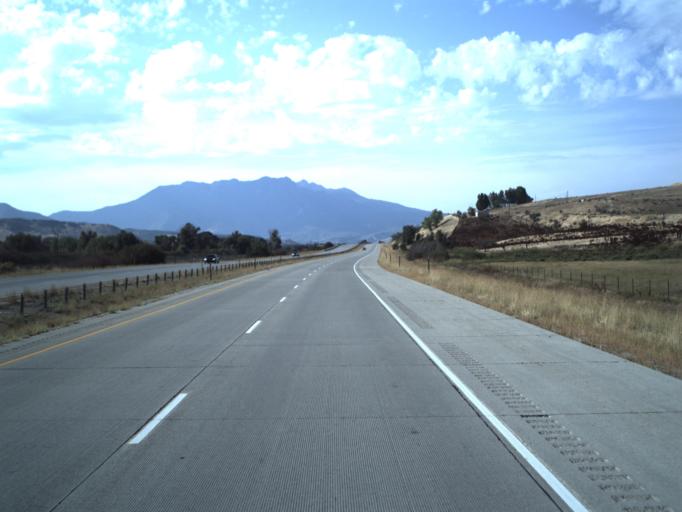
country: US
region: Utah
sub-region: Morgan County
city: Morgan
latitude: 41.0805
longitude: -111.7265
